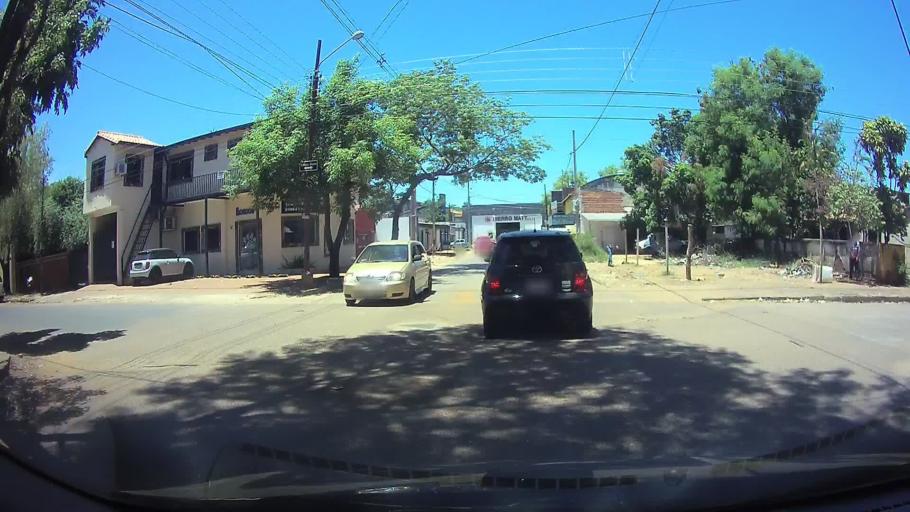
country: PY
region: Central
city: San Lorenzo
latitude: -25.2717
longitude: -57.4854
